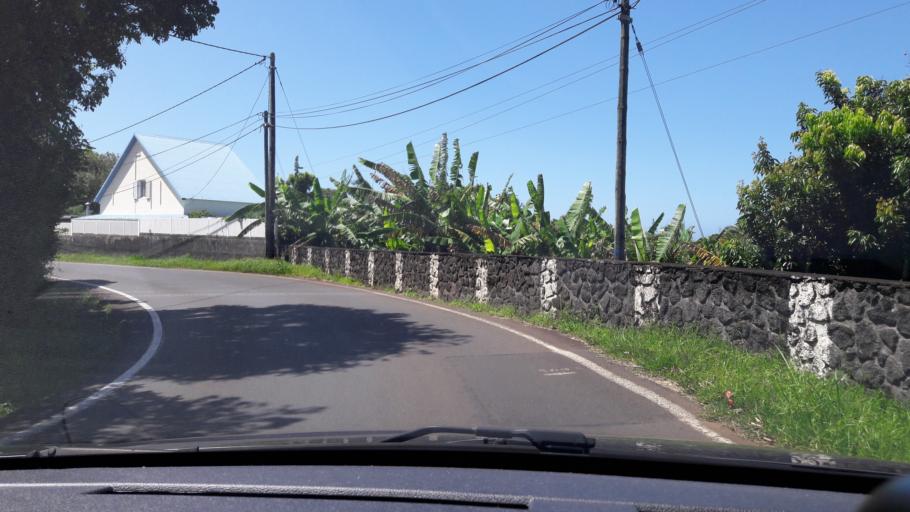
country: RE
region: Reunion
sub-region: Reunion
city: Saint-Benoit
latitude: -21.0953
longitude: 55.7078
